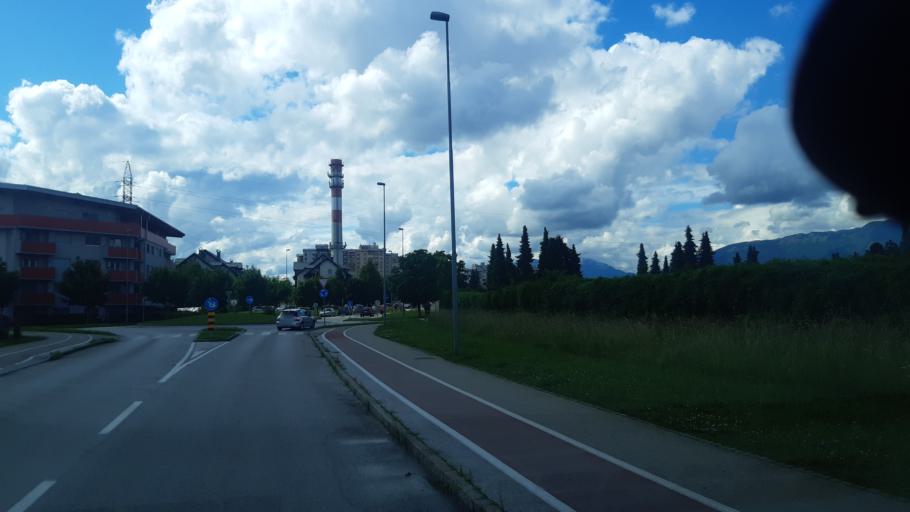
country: SI
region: Kranj
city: Kranj
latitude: 46.2330
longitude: 14.3687
